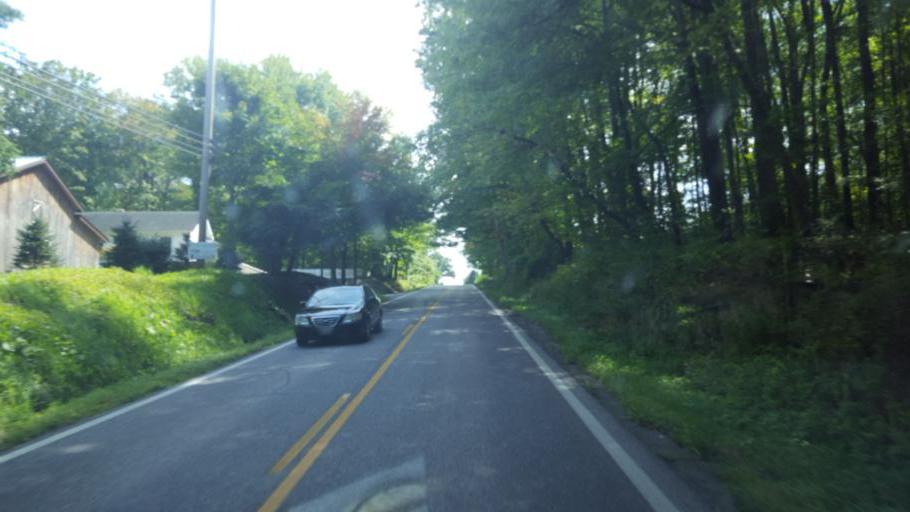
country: US
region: Ohio
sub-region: Geauga County
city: Burton
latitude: 41.4521
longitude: -81.1360
